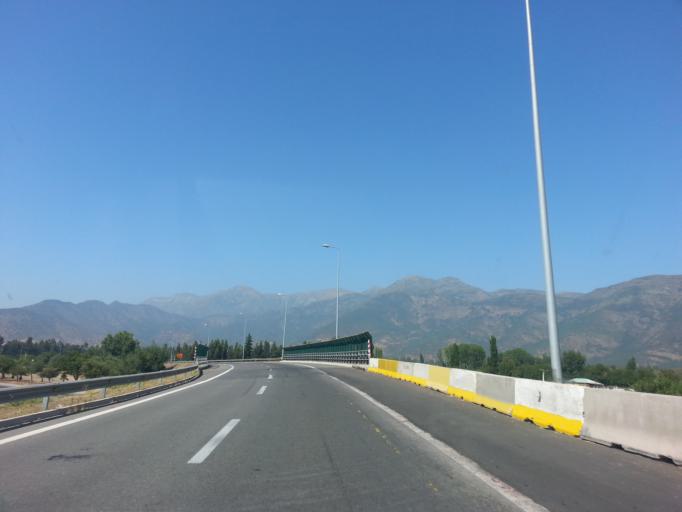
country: CL
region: Santiago Metropolitan
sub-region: Provincia de Maipo
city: Paine
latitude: -33.8800
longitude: -70.7357
